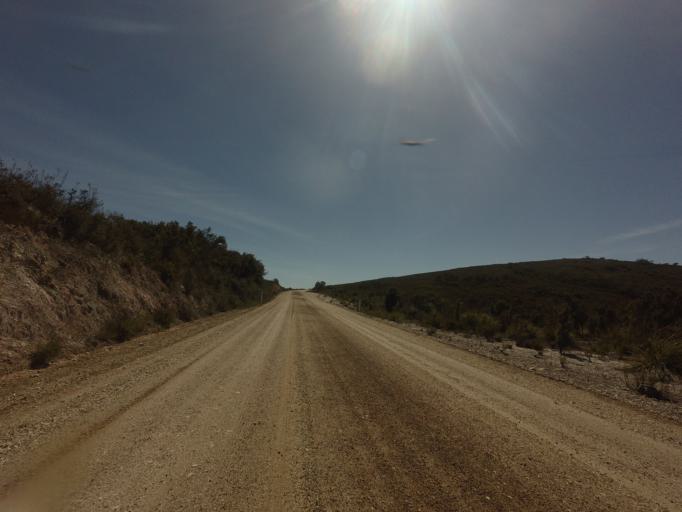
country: AU
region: Tasmania
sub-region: Huon Valley
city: Geeveston
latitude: -43.0349
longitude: 146.3335
